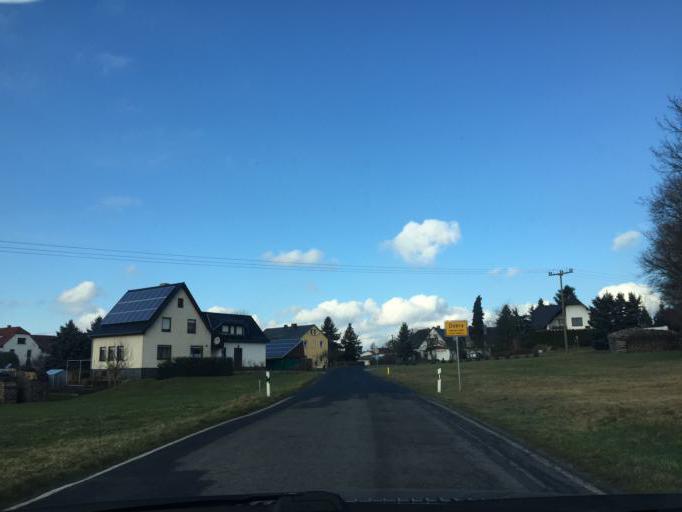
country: DE
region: Saxony
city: Tauscha
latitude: 51.2561
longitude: 13.7742
